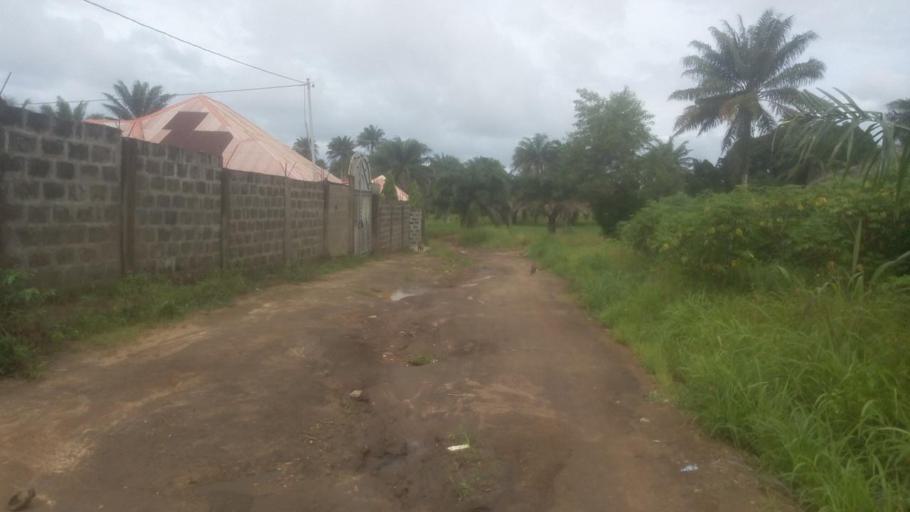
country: SL
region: Northern Province
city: Masoyila
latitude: 8.5945
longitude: -13.1848
